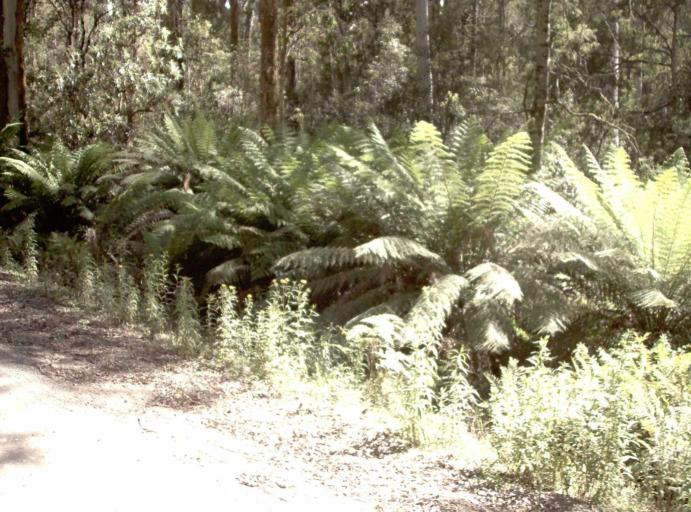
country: AU
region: New South Wales
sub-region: Bombala
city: Bombala
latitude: -37.2333
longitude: 148.7539
